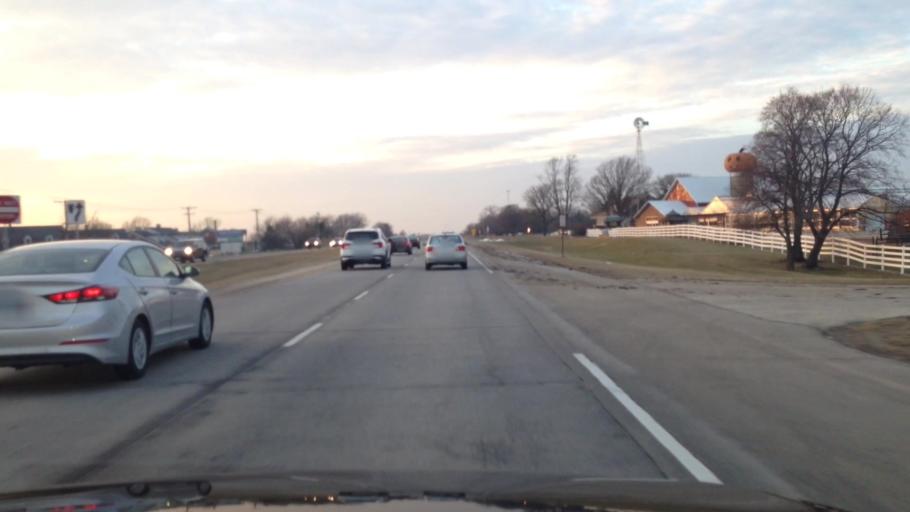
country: US
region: Illinois
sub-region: Cook County
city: Streamwood
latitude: 42.0678
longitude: -88.1654
